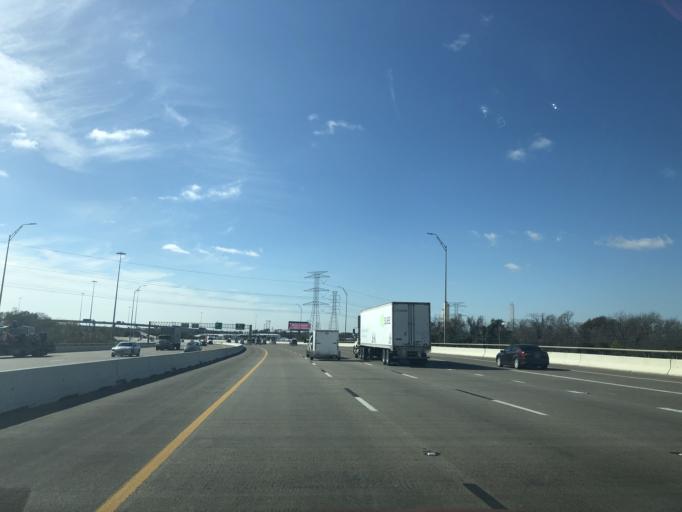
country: US
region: Texas
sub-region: Harris County
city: La Porte
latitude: 29.6963
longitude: -95.0267
